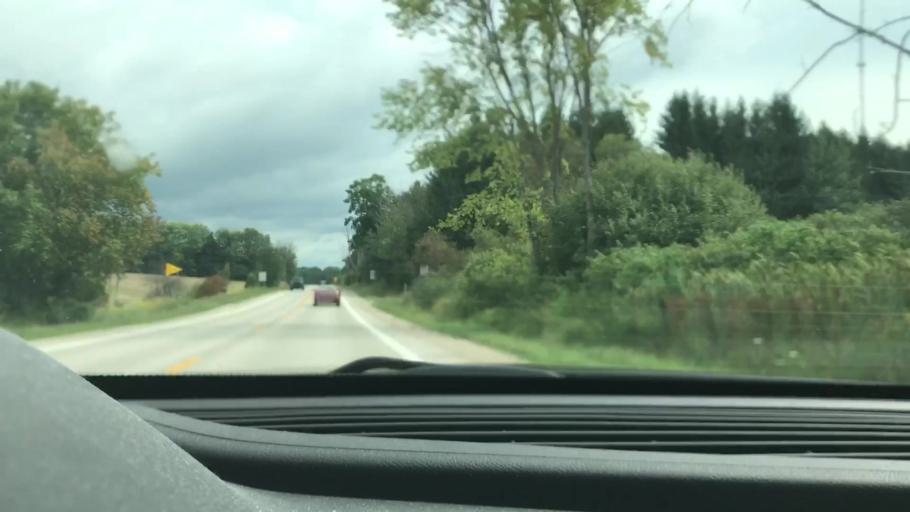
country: US
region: Michigan
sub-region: Antrim County
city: Bellaire
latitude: 45.0956
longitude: -85.2967
